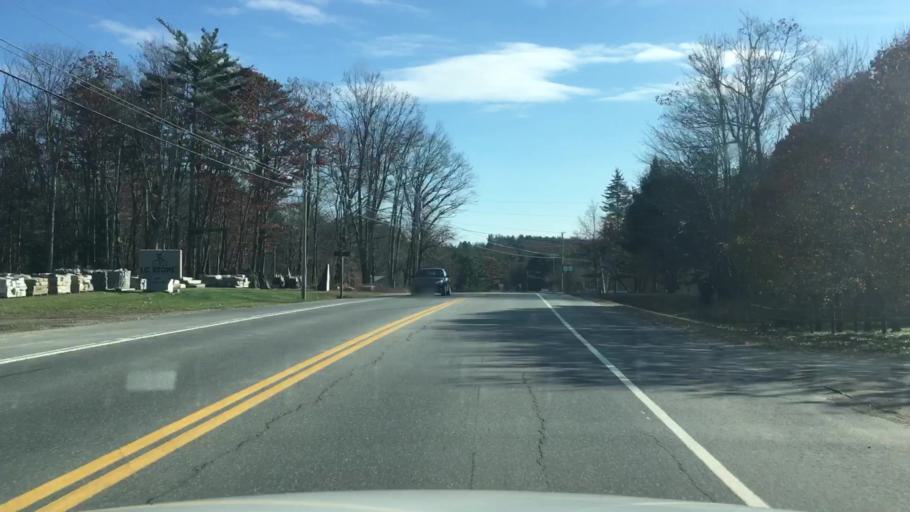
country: US
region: Maine
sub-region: Kennebec County
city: Windsor
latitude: 44.2525
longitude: -69.5421
